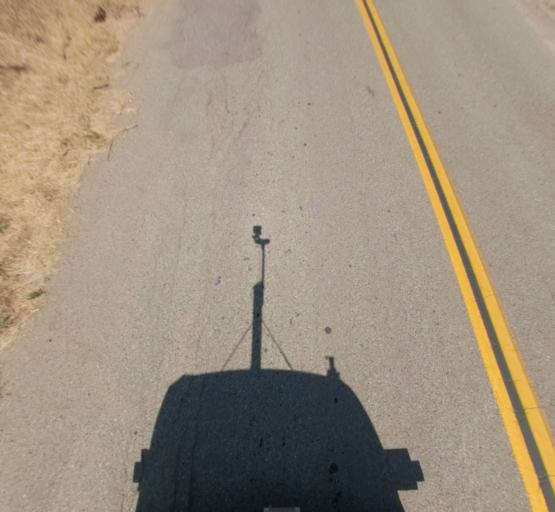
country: US
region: California
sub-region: Fresno County
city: Auberry
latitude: 37.2362
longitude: -119.4709
